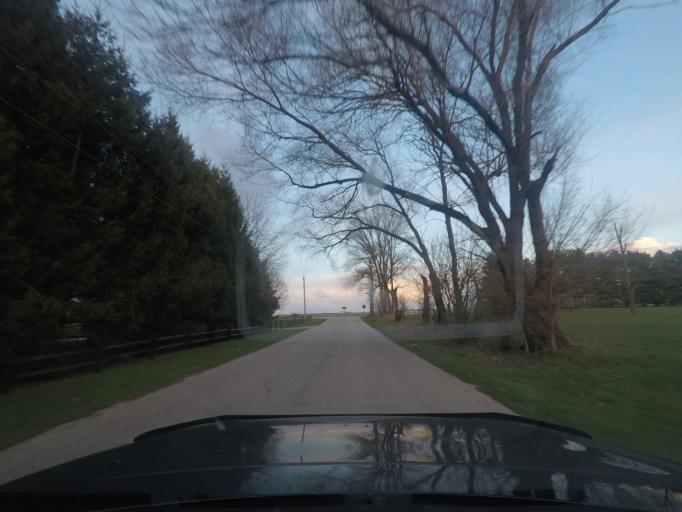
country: US
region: Indiana
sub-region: LaPorte County
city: Kingsford Heights
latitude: 41.4620
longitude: -86.7053
